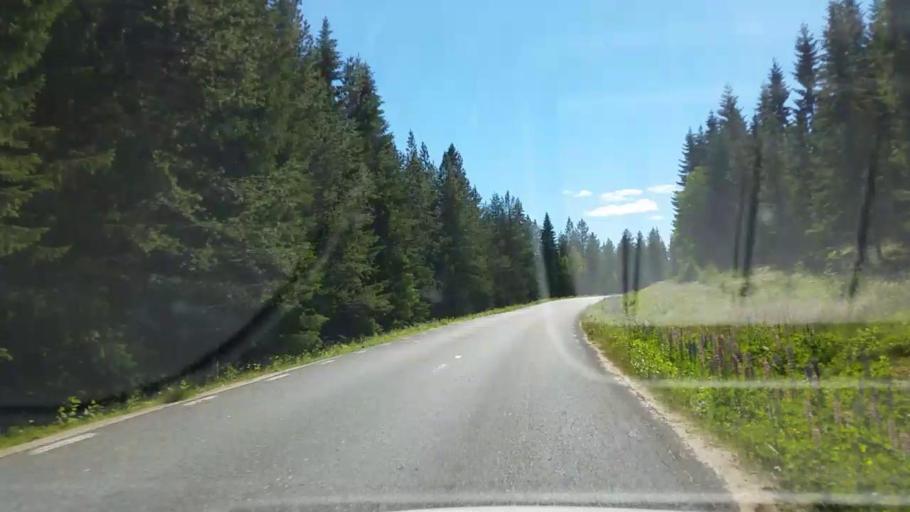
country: SE
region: Gaevleborg
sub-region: Ljusdals Kommun
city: Farila
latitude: 61.6607
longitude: 15.6043
